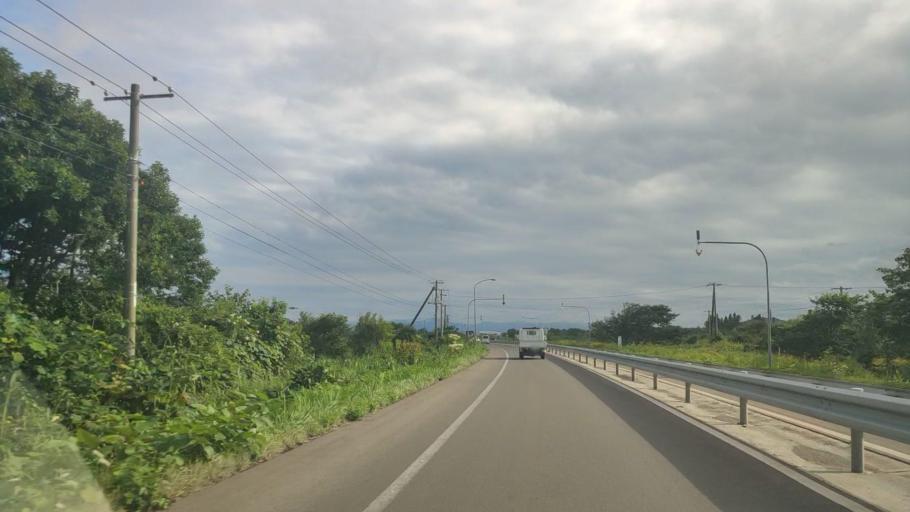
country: JP
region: Hokkaido
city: Niseko Town
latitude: 42.4554
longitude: 140.3330
